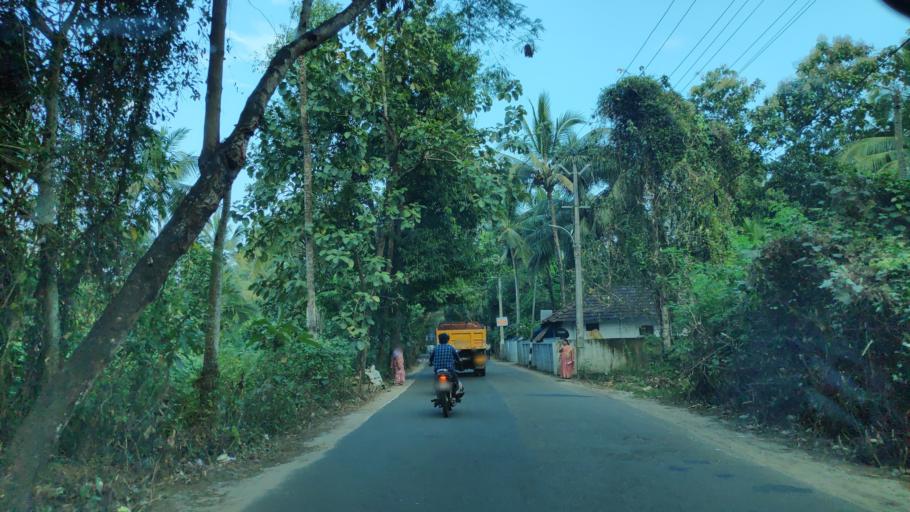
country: IN
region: Kerala
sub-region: Alappuzha
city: Shertallai
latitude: 9.6739
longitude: 76.3909
